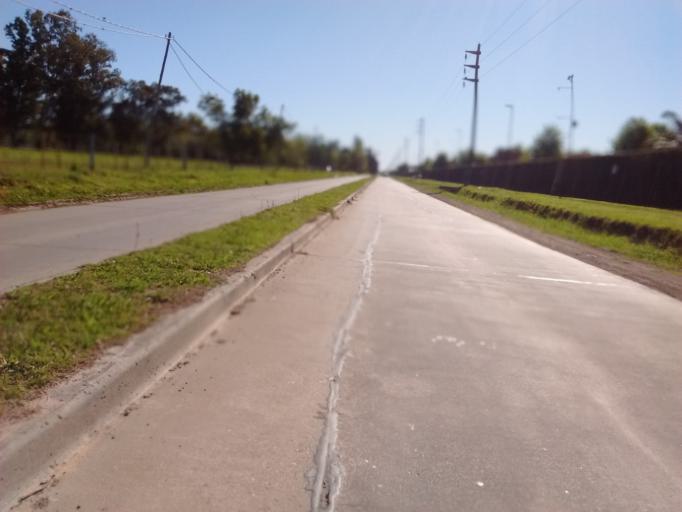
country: AR
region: Santa Fe
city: Funes
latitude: -32.9300
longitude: -60.8341
